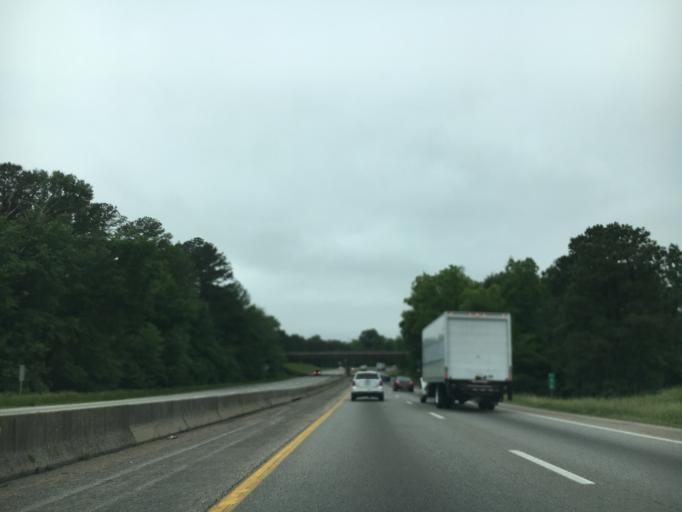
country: US
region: Virginia
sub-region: City of Petersburg
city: Petersburg
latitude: 37.1992
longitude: -77.4243
